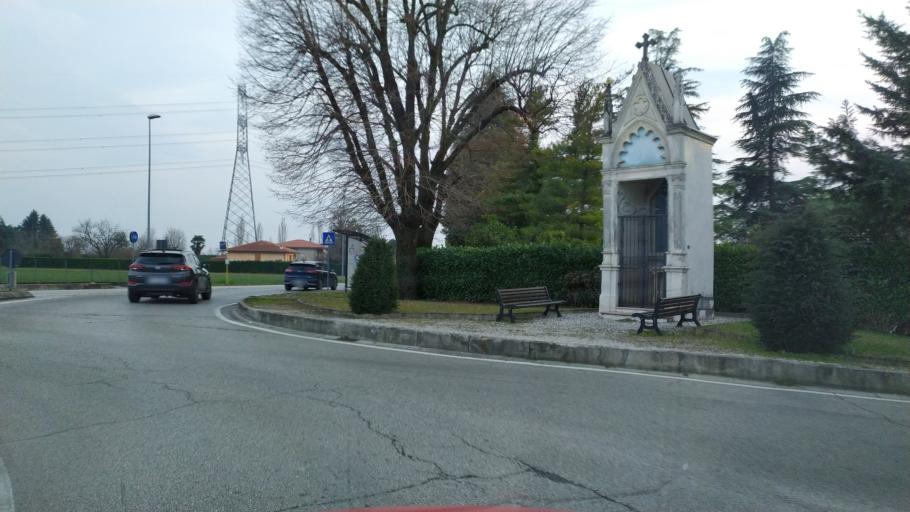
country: IT
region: Veneto
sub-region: Provincia di Vicenza
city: Montecchio Precalcino
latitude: 45.6585
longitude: 11.5579
